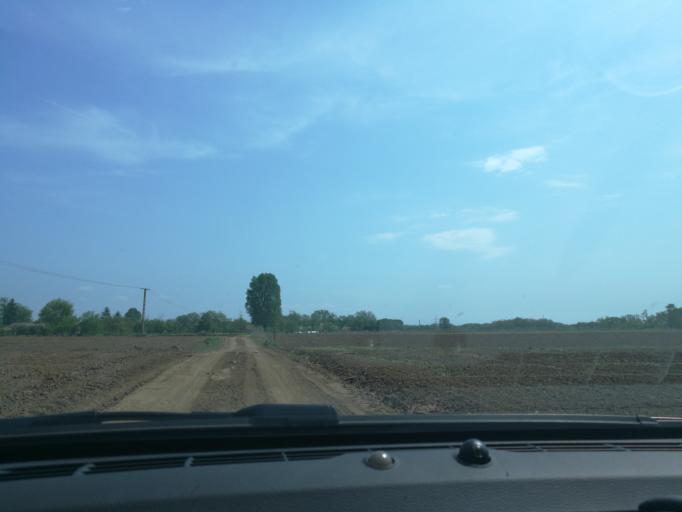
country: HU
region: Szabolcs-Szatmar-Bereg
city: Nyirtelek
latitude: 47.9703
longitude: 21.6549
